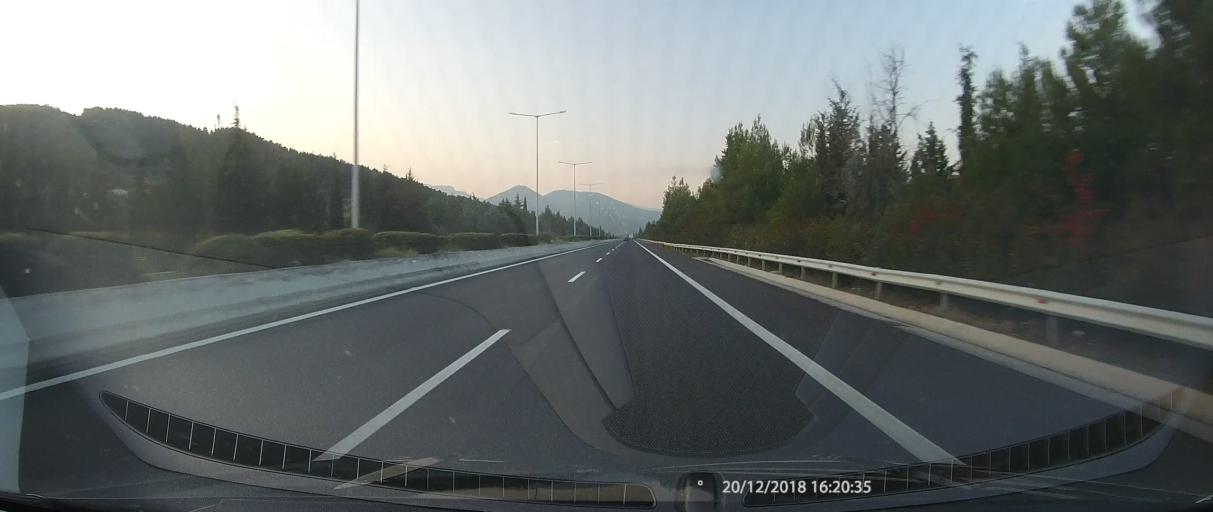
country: GR
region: Thessaly
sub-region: Nomos Magnisias
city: Pteleos
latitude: 39.0322
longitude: 22.9071
